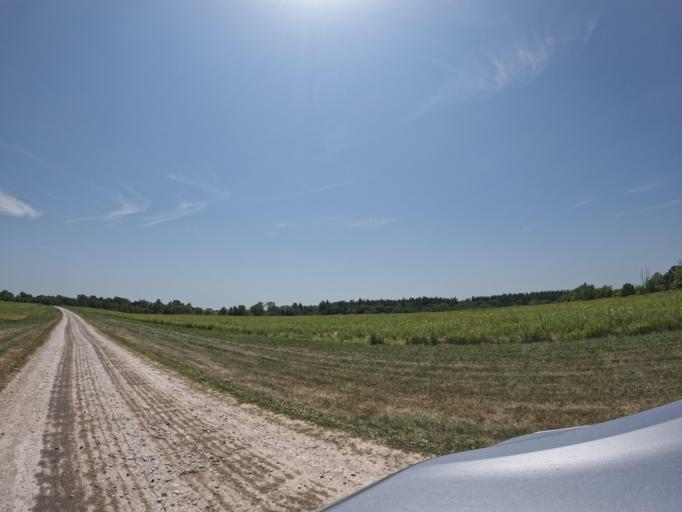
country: US
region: Iowa
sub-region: Henry County
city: Mount Pleasant
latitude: 40.9409
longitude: -91.5868
